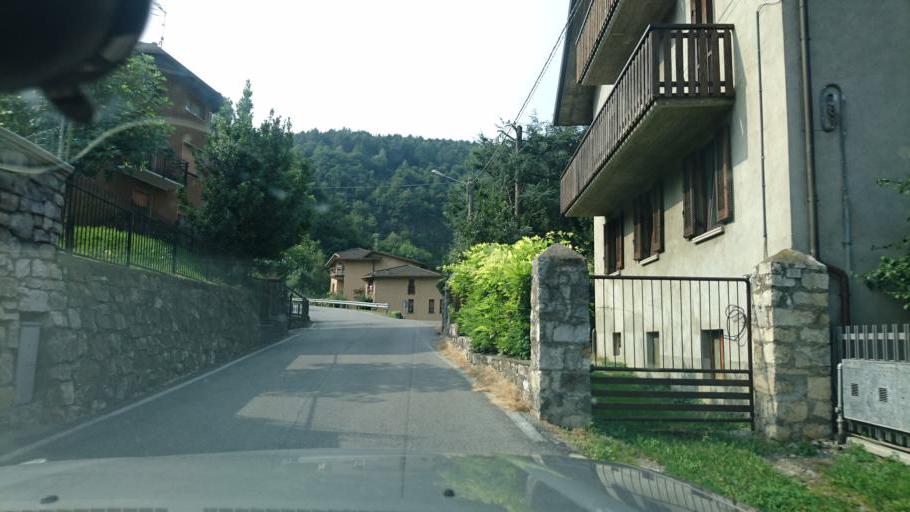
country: IT
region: Lombardy
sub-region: Provincia di Brescia
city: Breno
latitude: 45.9534
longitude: 10.3056
